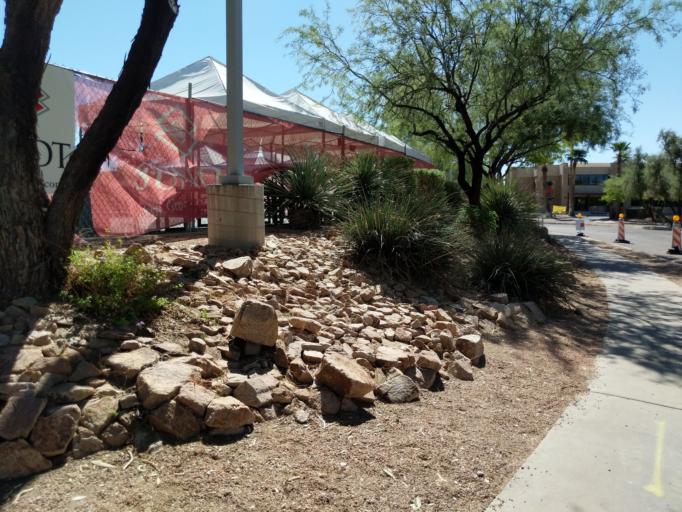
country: US
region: Arizona
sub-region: Pima County
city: Tucson
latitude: 32.2170
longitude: -110.8803
